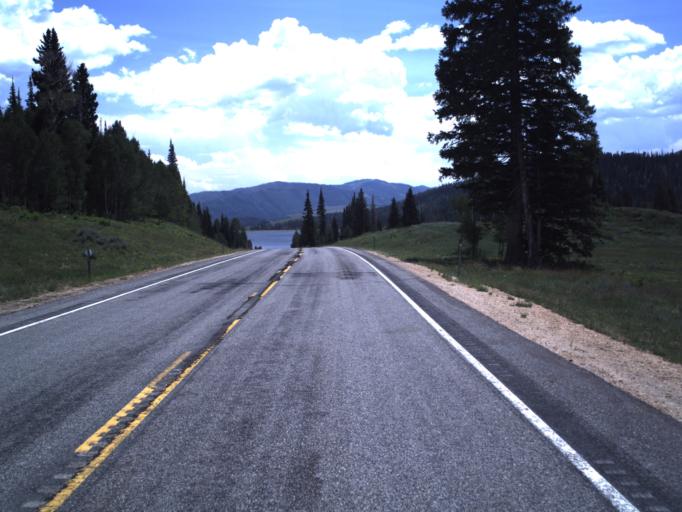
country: US
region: Utah
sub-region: Sanpete County
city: Fairview
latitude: 39.6018
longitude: -111.2735
